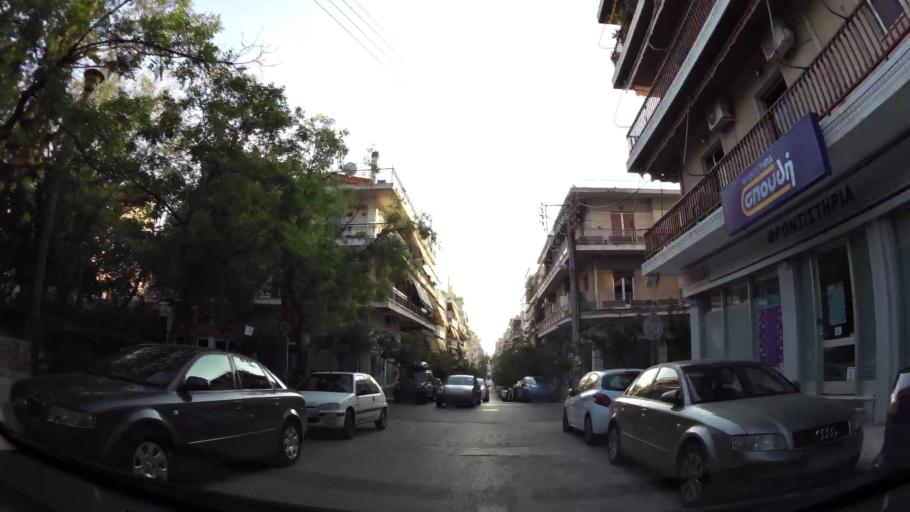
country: GR
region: Attica
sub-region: Nomarchia Athinas
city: Galatsi
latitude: 38.0255
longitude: 23.7479
